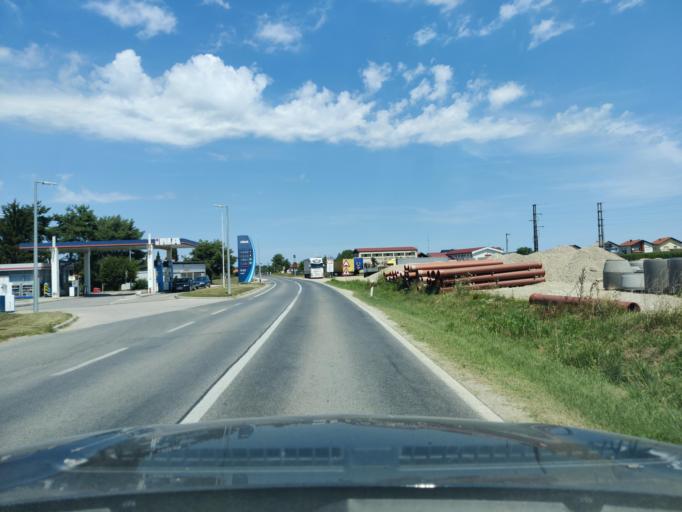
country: HR
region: Medimurska
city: Vratisinec
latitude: 46.5026
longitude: 16.4310
